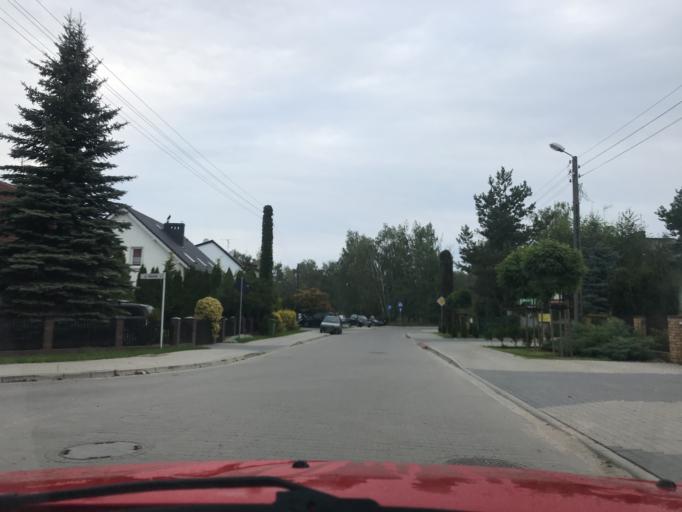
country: PL
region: Greater Poland Voivodeship
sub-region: Powiat poznanski
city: Plewiska
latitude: 52.3918
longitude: 16.7985
